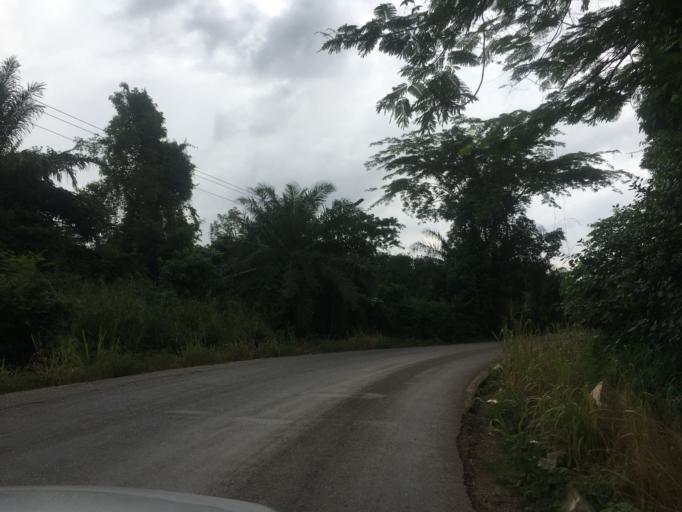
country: GH
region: Ashanti
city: Mamponteng
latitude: 6.6819
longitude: -1.5622
